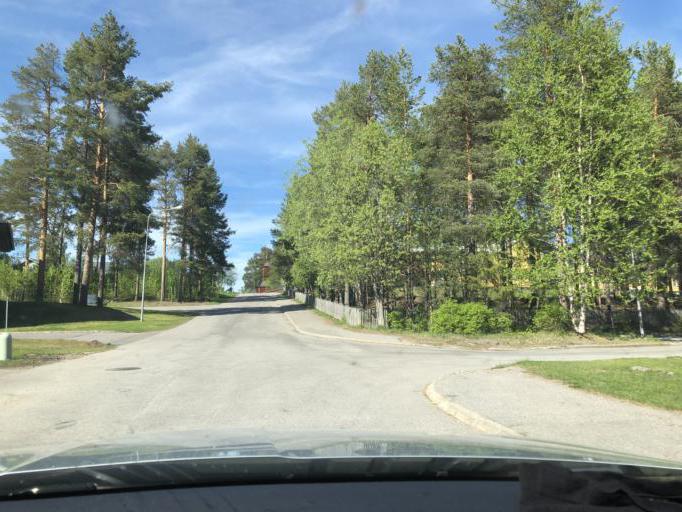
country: SE
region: Norrbotten
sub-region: Jokkmokks Kommun
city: Jokkmokk
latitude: 66.6027
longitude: 19.8286
